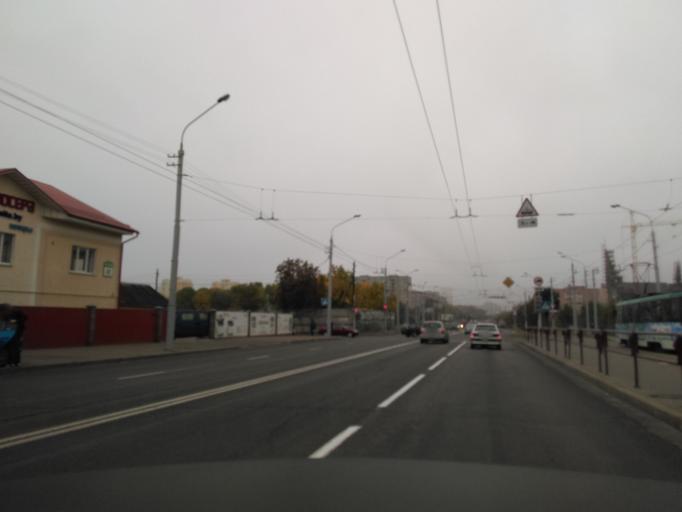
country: BY
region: Minsk
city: Minsk
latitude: 53.8675
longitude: 27.6201
